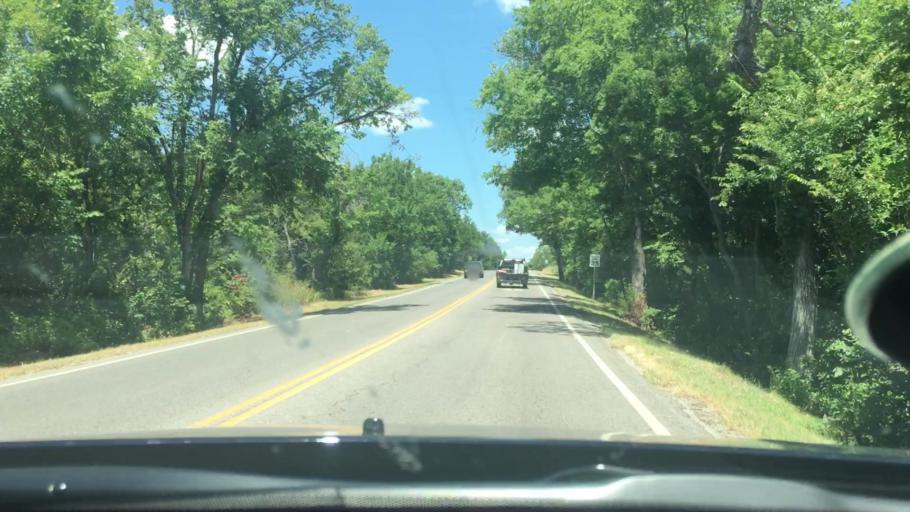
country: US
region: Oklahoma
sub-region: Murray County
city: Sulphur
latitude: 34.4939
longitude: -96.9679
